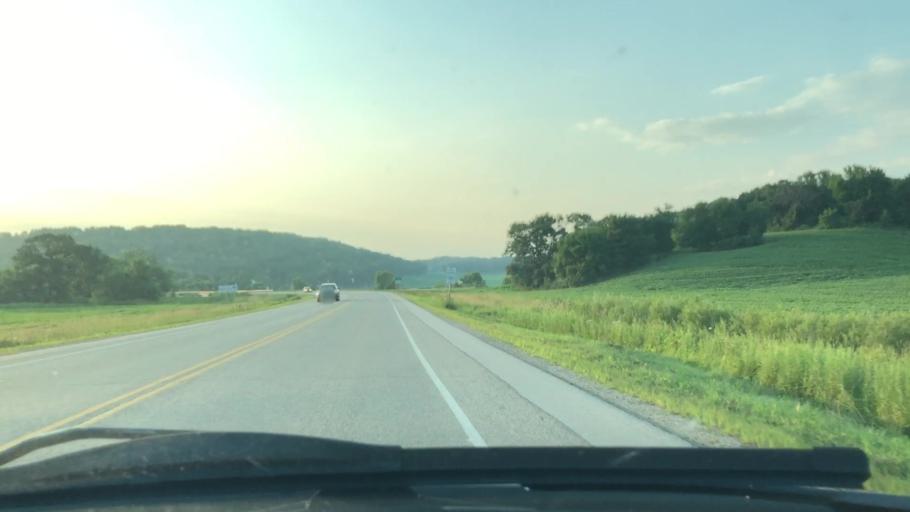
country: US
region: Wisconsin
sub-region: Dane County
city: Black Earth
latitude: 43.1389
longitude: -89.7406
